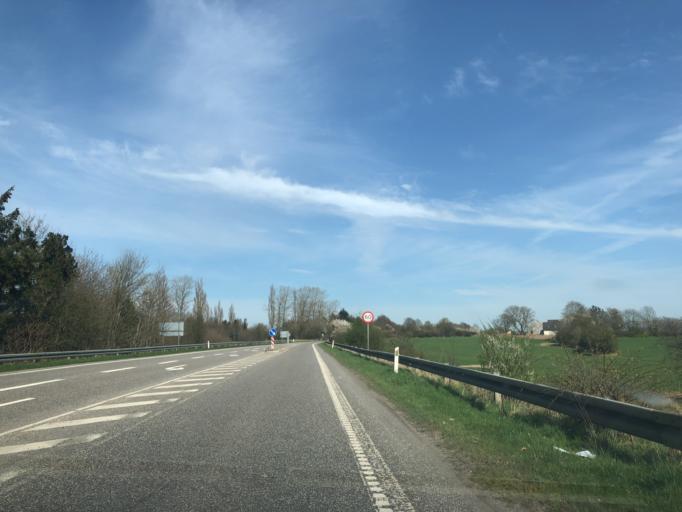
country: DK
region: Zealand
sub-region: Faxe Kommune
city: Fakse
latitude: 55.2673
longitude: 12.1080
